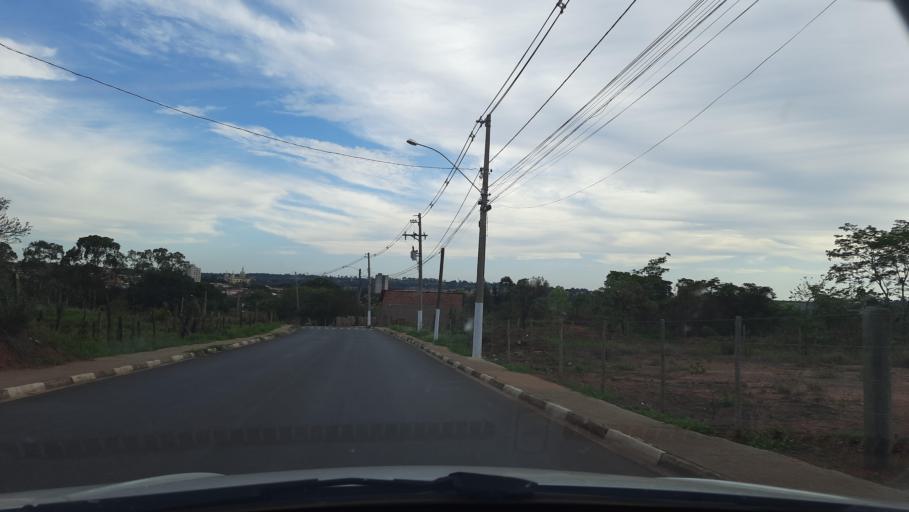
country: BR
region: Sao Paulo
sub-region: Casa Branca
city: Casa Branca
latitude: -21.7625
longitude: -47.0855
